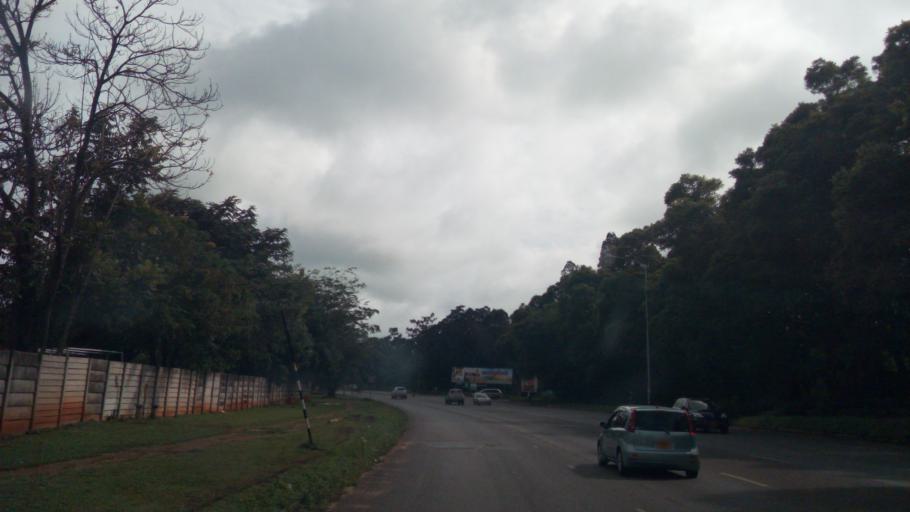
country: ZW
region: Harare
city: Harare
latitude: -17.8064
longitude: 31.0589
